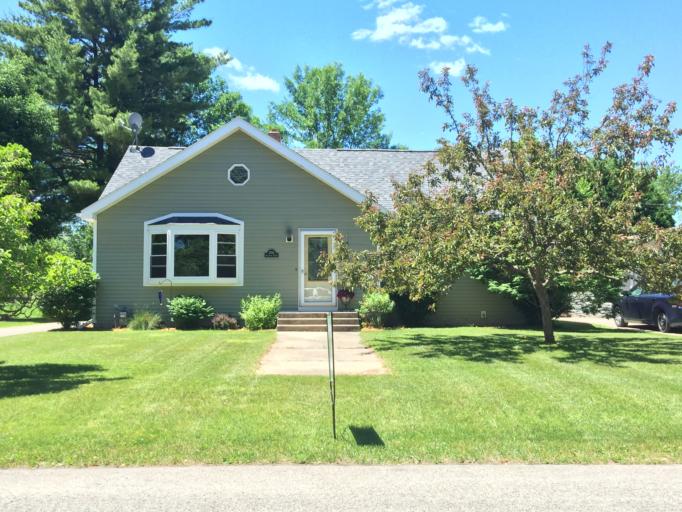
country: US
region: Michigan
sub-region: Menominee County
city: Menominee
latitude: 45.1327
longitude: -87.6214
